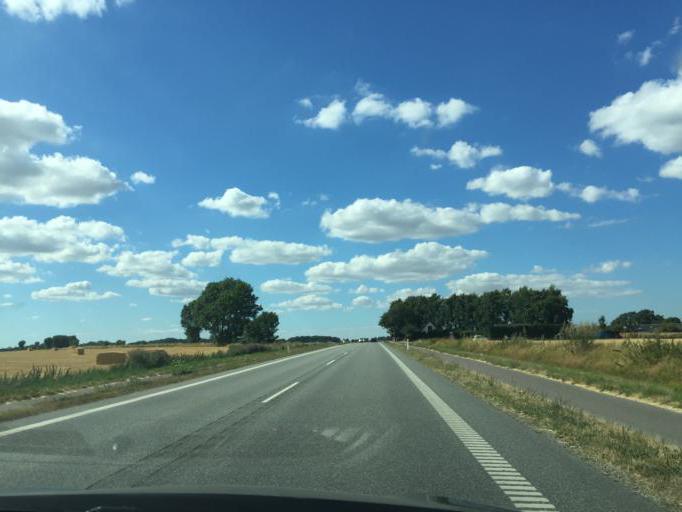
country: DK
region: South Denmark
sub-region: Odense Kommune
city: Hojby
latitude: 55.3343
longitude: 10.3895
